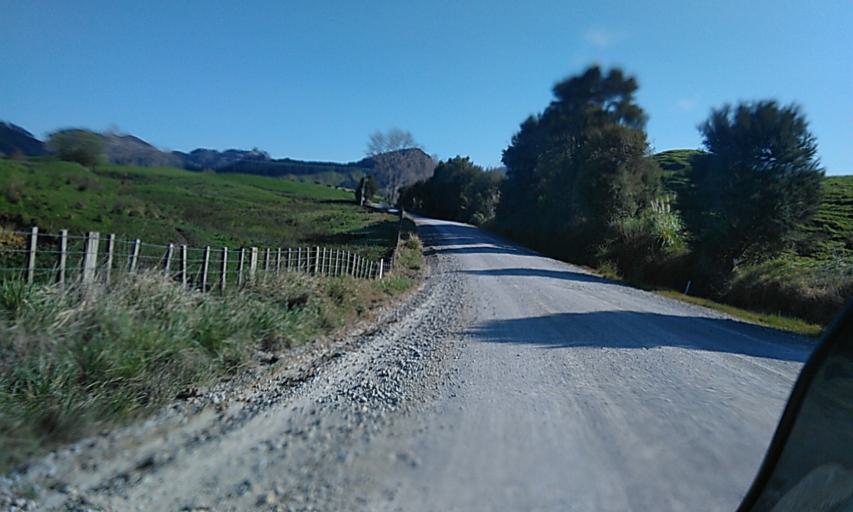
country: NZ
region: Gisborne
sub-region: Gisborne District
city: Gisborne
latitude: -38.4937
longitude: 178.0594
